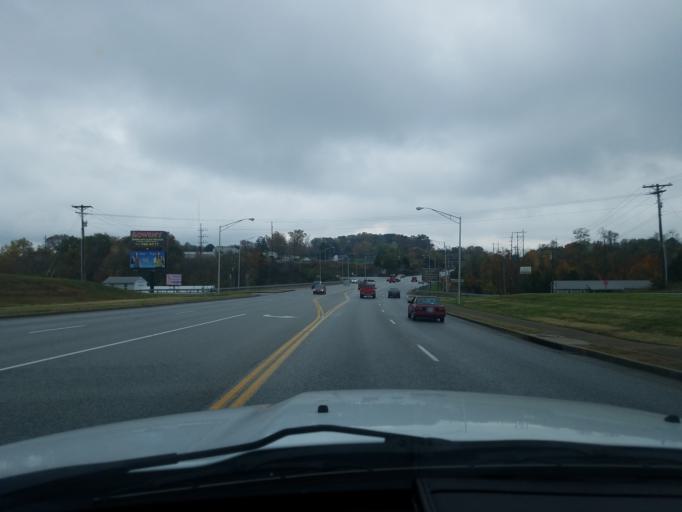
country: US
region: Kentucky
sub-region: Taylor County
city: Campbellsville
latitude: 37.3403
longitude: -85.3616
